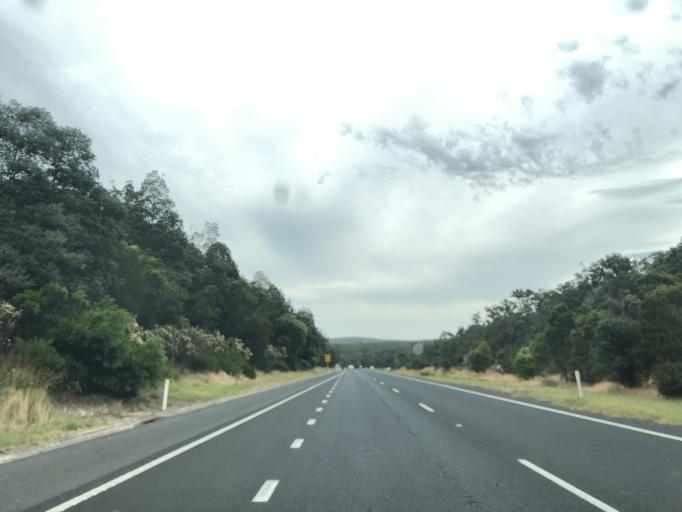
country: AU
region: Victoria
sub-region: Hume
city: Sunbury
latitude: -37.4198
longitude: 144.5434
